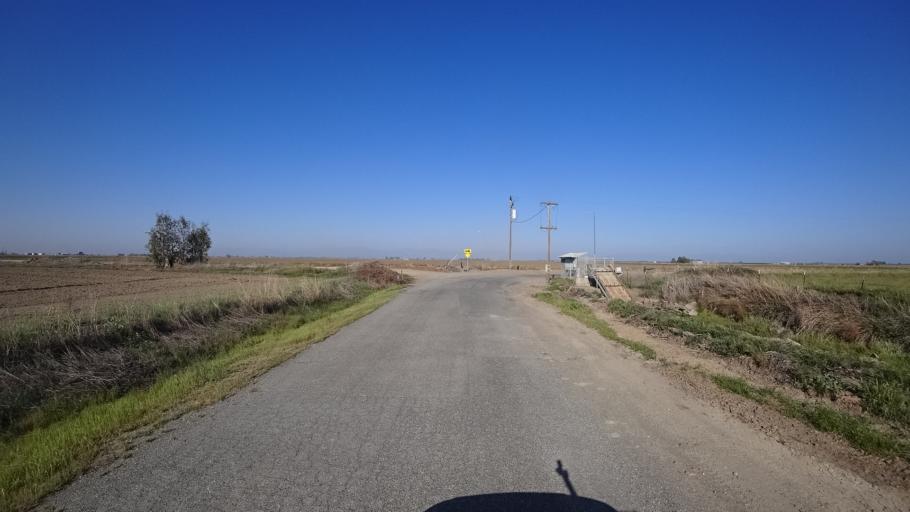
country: US
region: California
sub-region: Glenn County
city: Willows
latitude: 39.5585
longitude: -122.1073
